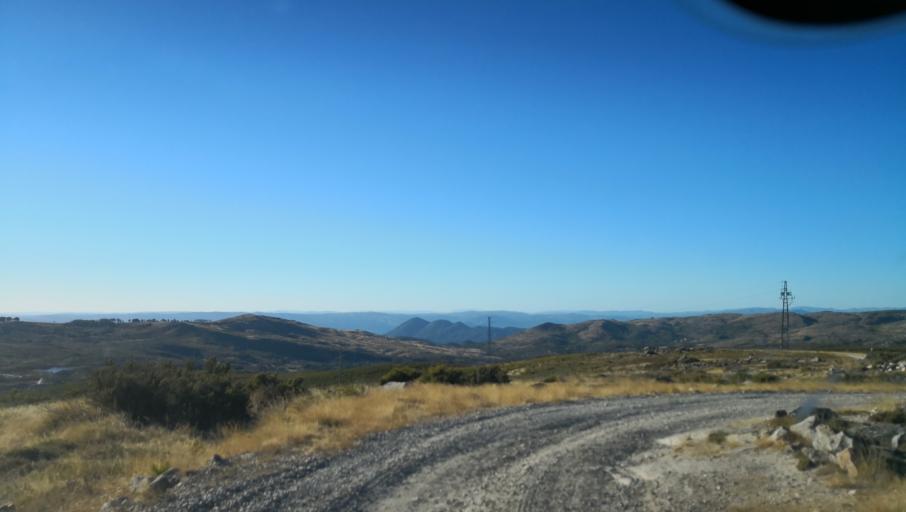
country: PT
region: Vila Real
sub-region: Vila Real
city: Vila Real
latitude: 41.3567
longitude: -7.7738
